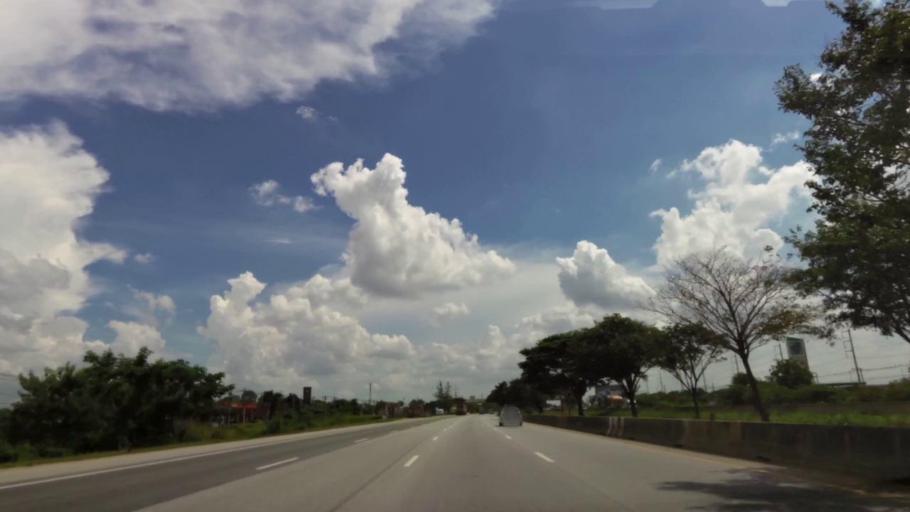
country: TH
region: Phra Nakhon Si Ayutthaya
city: Maha Rat
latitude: 14.5089
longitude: 100.5185
